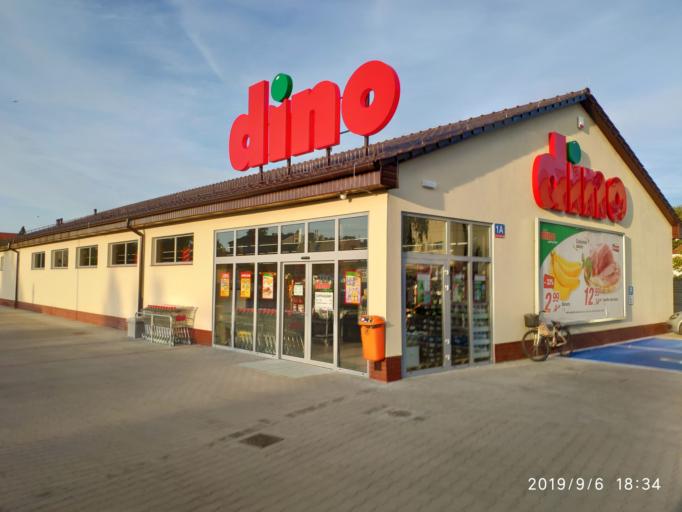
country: PL
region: Lubusz
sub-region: Powiat wschowski
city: Wschowa
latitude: 51.8012
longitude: 16.3139
